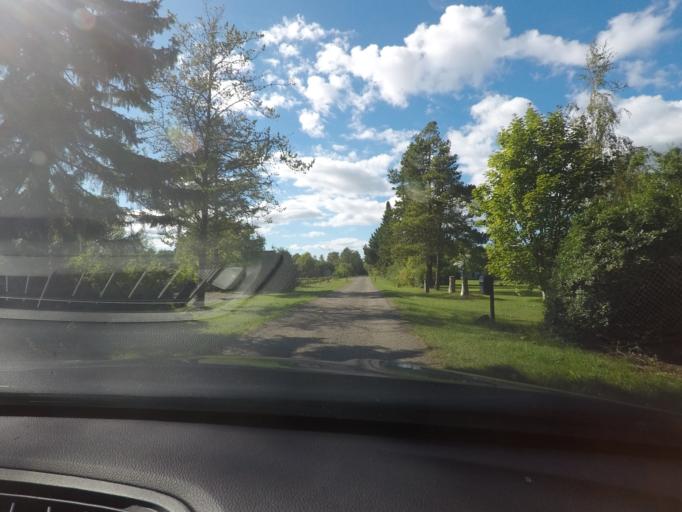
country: DK
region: Zealand
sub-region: Guldborgsund Kommune
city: Sakskobing
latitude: 54.9712
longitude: 11.5624
